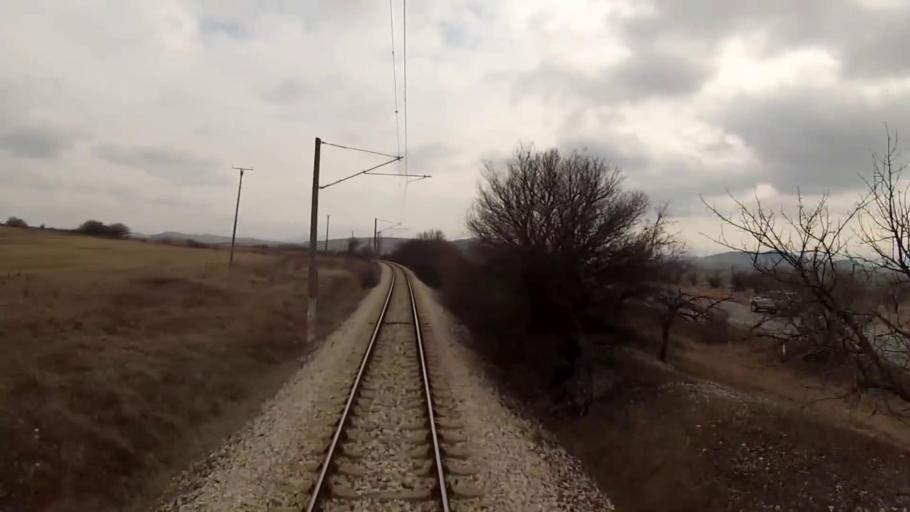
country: BG
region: Sofiya
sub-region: Obshtina Gorna Malina
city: Gorna Malina
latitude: 42.7015
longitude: 23.6764
